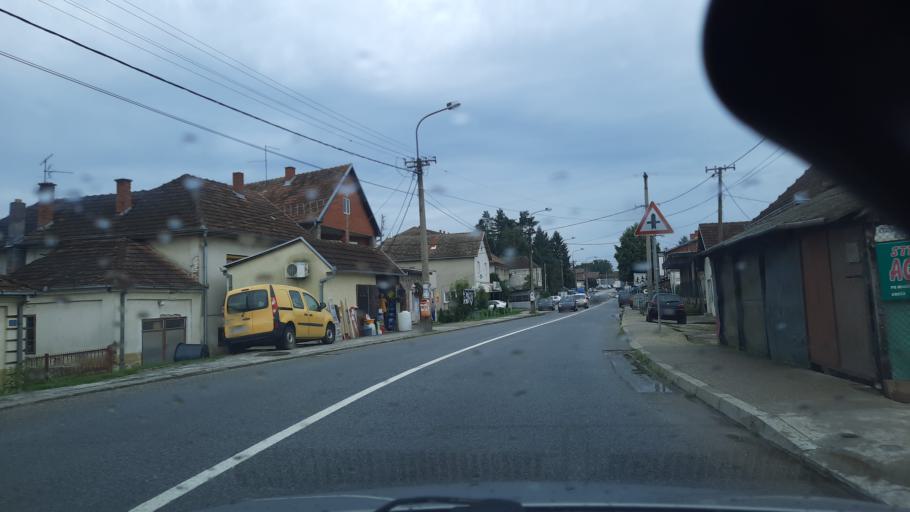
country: RS
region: Central Serbia
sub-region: Sumadijski Okrug
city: Knic
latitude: 43.8973
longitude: 20.7711
